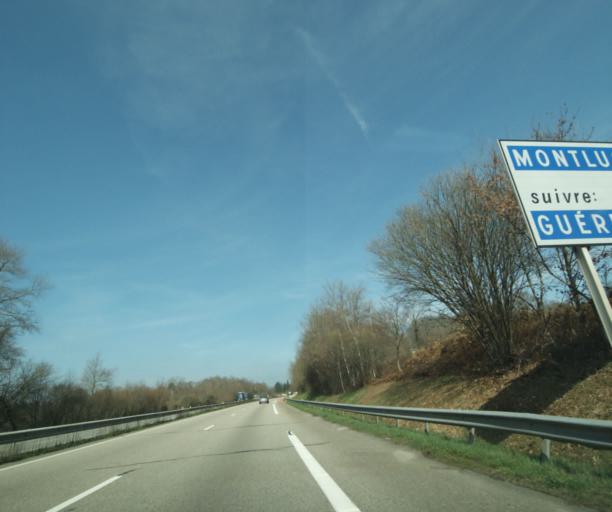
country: FR
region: Limousin
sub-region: Departement de la Haute-Vienne
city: Rilhac-Rancon
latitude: 45.9081
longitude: 1.2918
